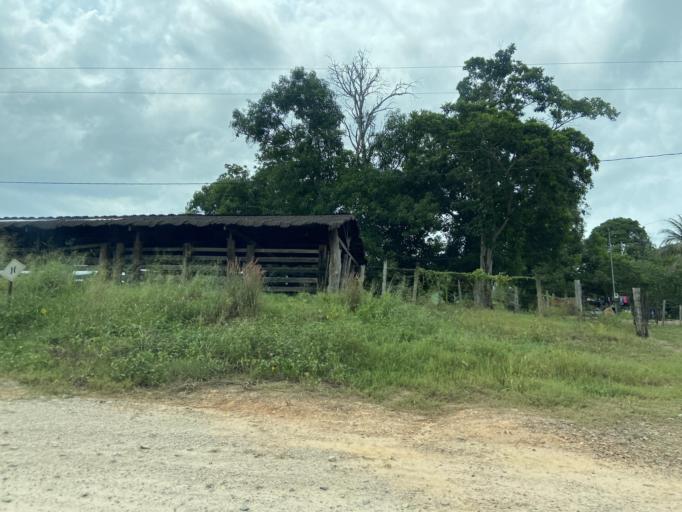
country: BR
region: Para
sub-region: Maraba
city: Maraba
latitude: -5.2544
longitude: -48.9797
